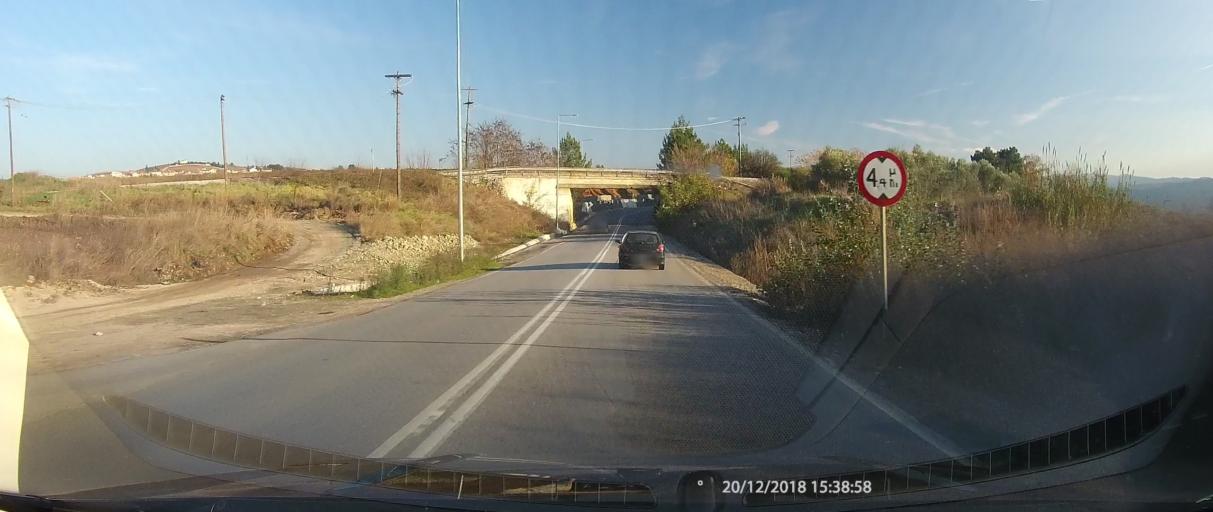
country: GR
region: Central Greece
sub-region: Nomos Fthiotidos
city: Stavros
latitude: 38.9000
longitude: 22.3585
